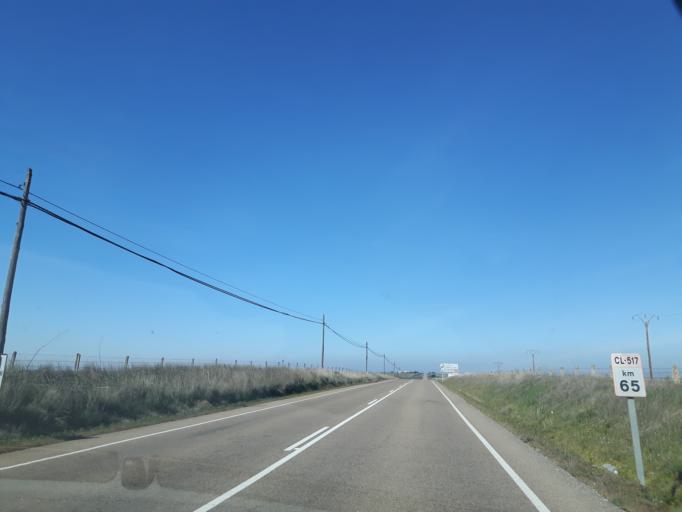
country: ES
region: Castille and Leon
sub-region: Provincia de Salamanca
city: Vitigudino
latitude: 41.0107
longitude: -6.4546
